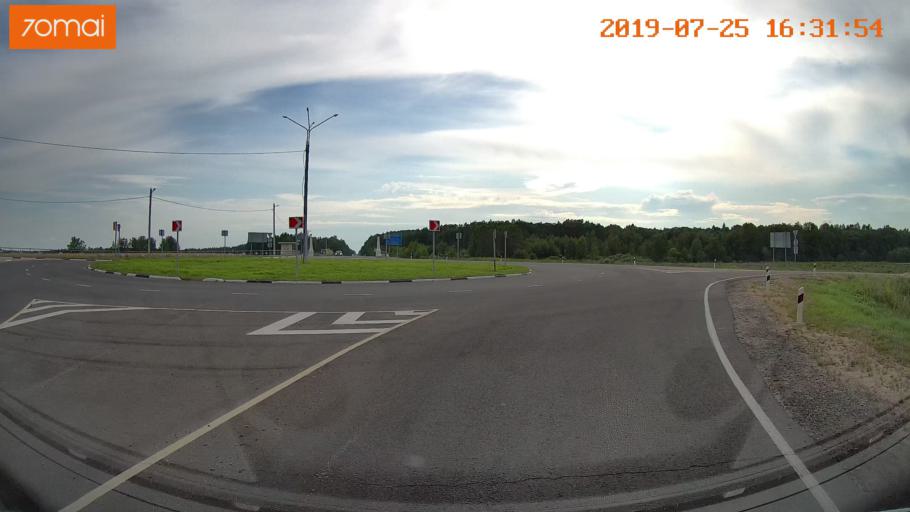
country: RU
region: Ivanovo
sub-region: Privolzhskiy Rayon
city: Ples
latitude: 57.4388
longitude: 41.4773
